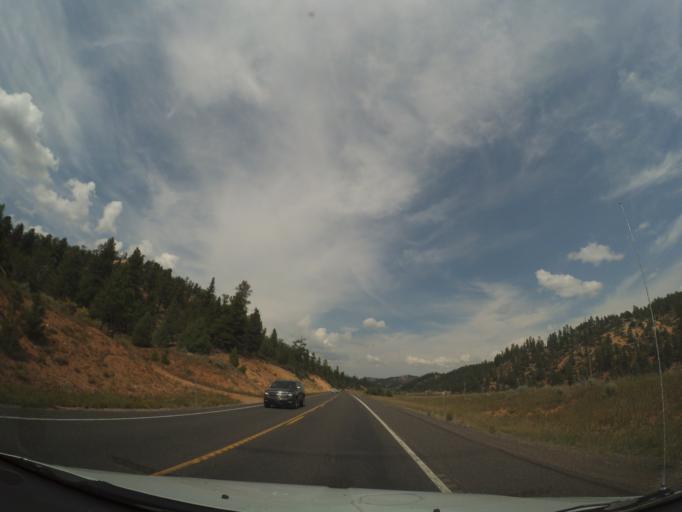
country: US
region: Utah
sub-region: Garfield County
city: Panguitch
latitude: 37.6229
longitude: -112.1735
